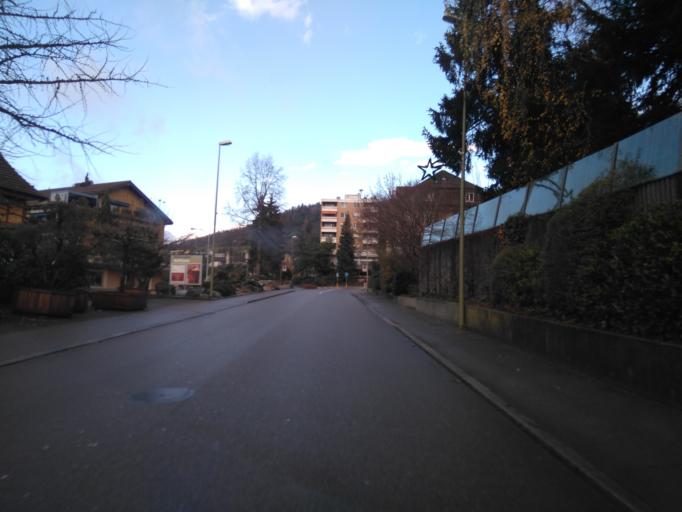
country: CH
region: Zurich
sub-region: Bezirk Dietikon
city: Unterengstringen
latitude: 47.4118
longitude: 8.4492
